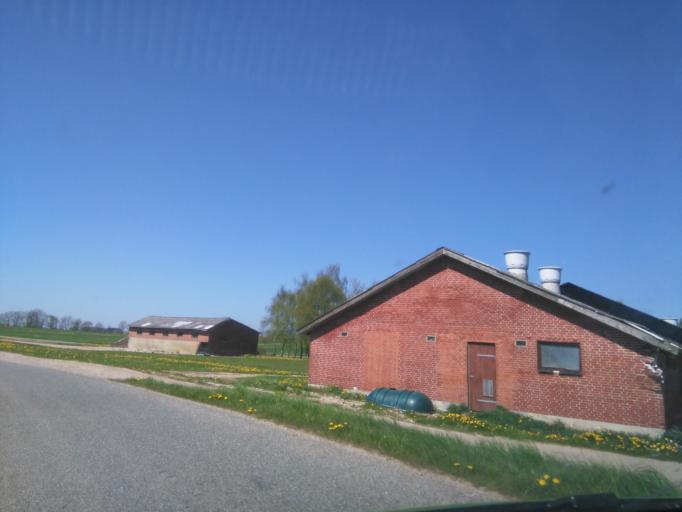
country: DK
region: Central Jutland
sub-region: Odder Kommune
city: Odder
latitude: 55.9032
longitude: 10.0450
